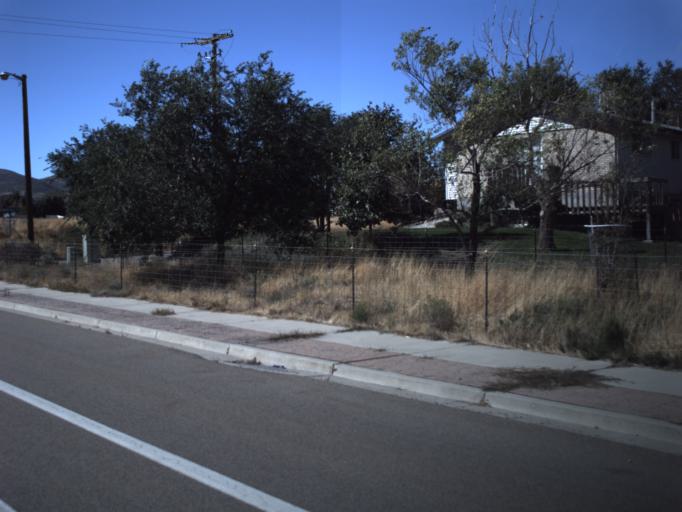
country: US
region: Utah
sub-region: Salt Lake County
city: Bluffdale
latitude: 40.4829
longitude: -111.9432
